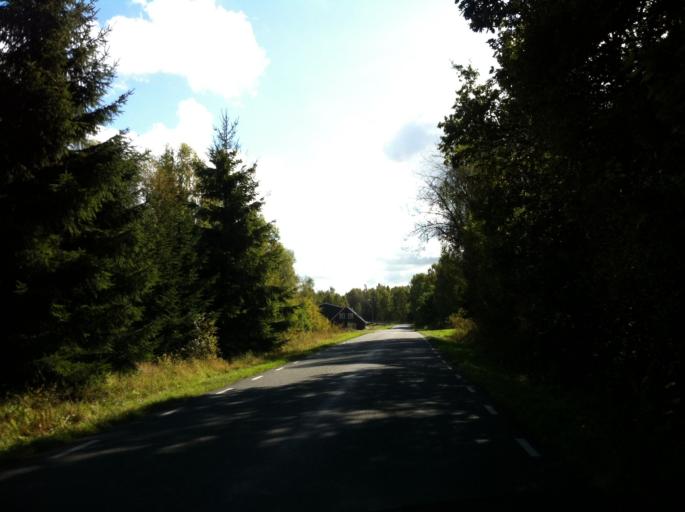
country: SE
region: Skane
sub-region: Kristianstads Kommun
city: Degeberga
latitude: 55.7440
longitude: 13.9409
